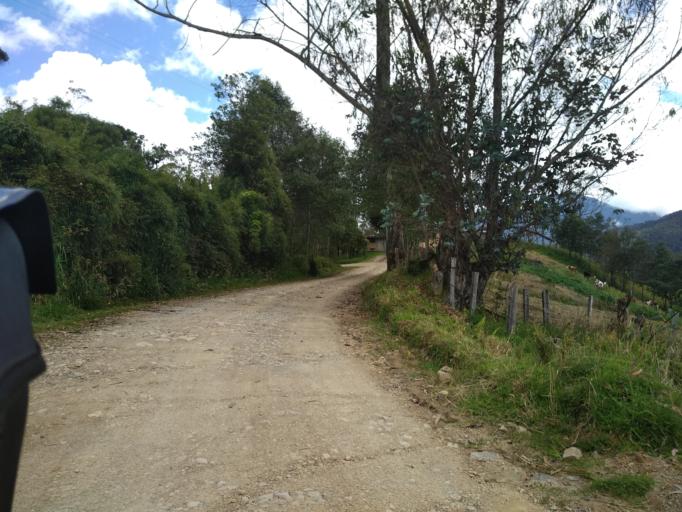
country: CO
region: Boyaca
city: Duitama
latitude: 5.9402
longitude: -73.1232
